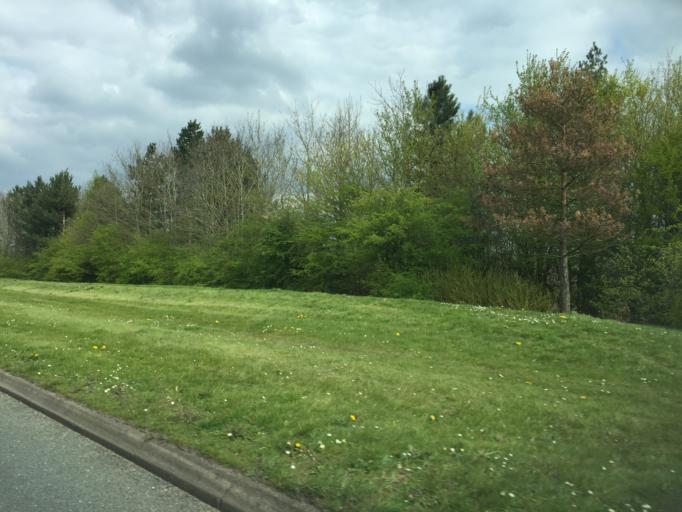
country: GB
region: England
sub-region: Milton Keynes
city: Shenley Church End
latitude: 52.0069
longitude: -0.7857
